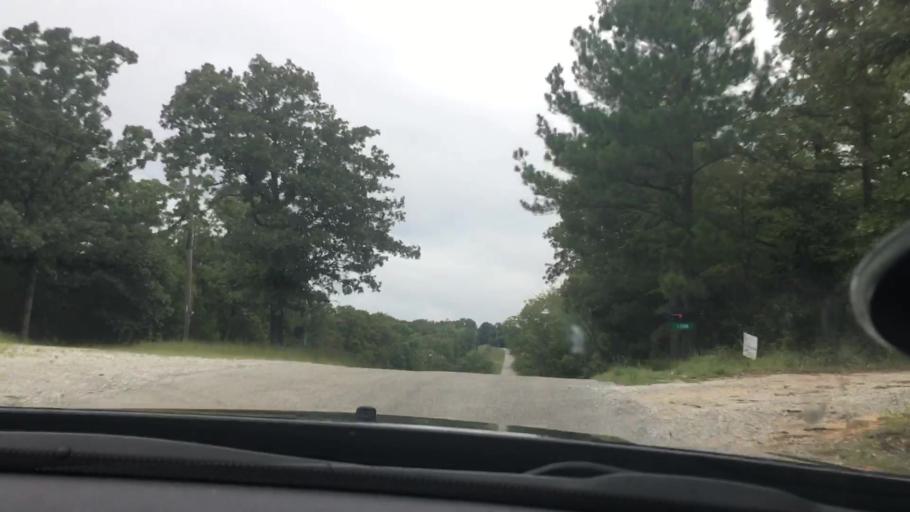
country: US
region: Oklahoma
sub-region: Pontotoc County
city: Byng
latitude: 34.8137
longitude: -96.5474
